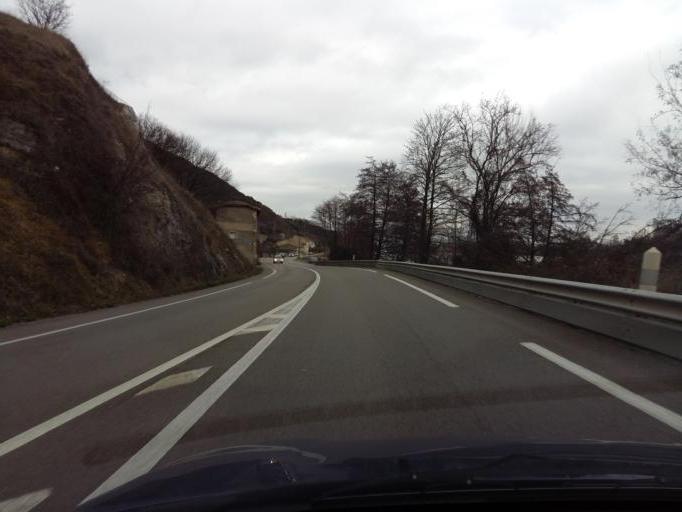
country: FR
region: Rhone-Alpes
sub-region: Departement de l'Ardeche
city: La Voulte-sur-Rhone
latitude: 44.7832
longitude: 4.7680
